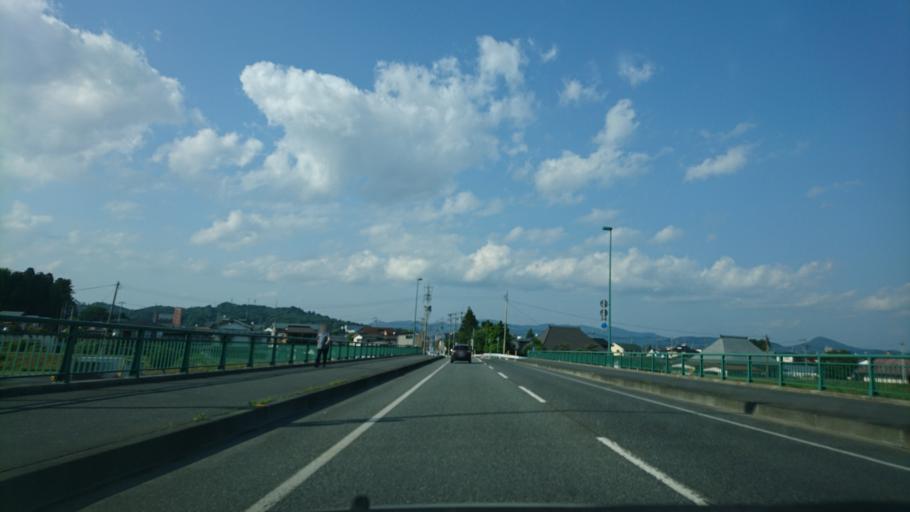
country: JP
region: Iwate
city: Ichinoseki
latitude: 38.9254
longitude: 141.1178
